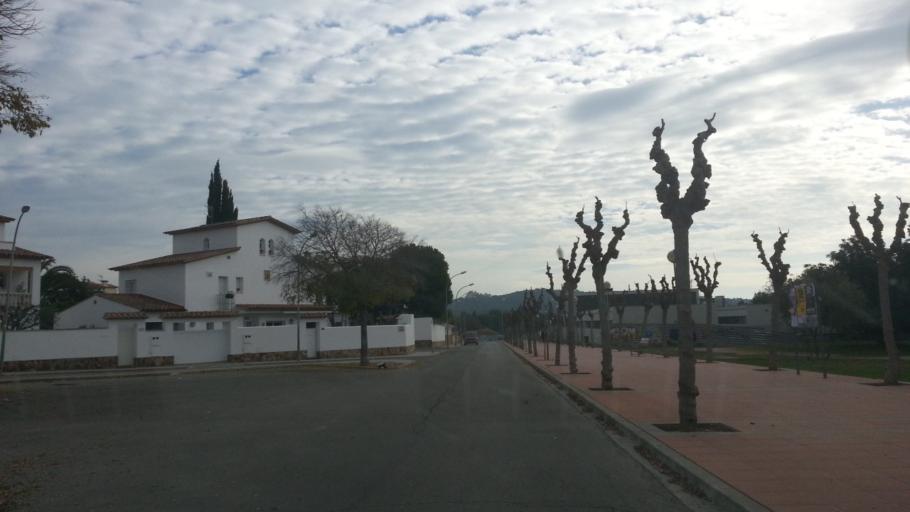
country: ES
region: Catalonia
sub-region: Provincia de Barcelona
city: Sant Pere de Ribes
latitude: 41.2559
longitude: 1.7729
